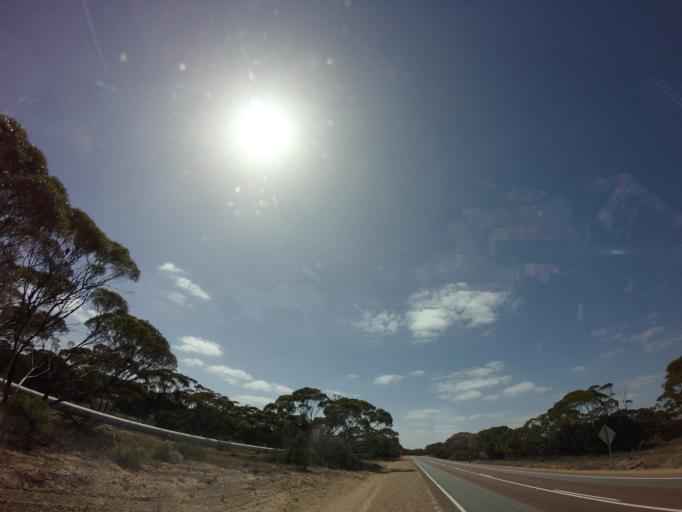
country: AU
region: South Australia
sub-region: Kimba
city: Caralue
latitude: -33.0895
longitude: 135.5098
